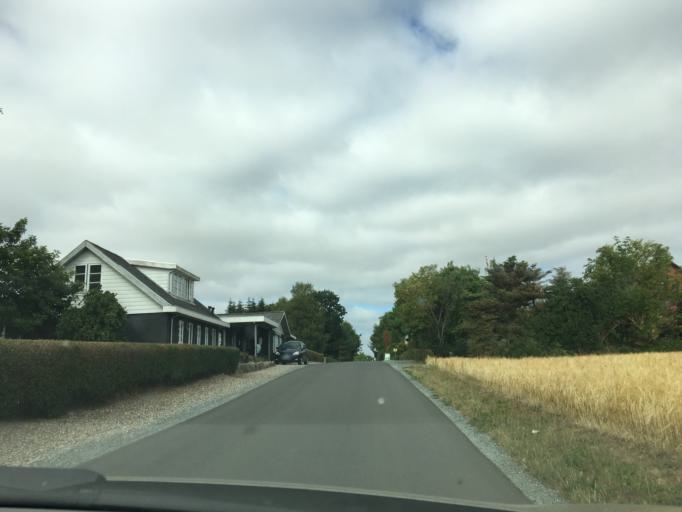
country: DK
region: South Denmark
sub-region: Middelfart Kommune
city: Norre Aby
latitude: 55.5067
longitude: 9.8636
